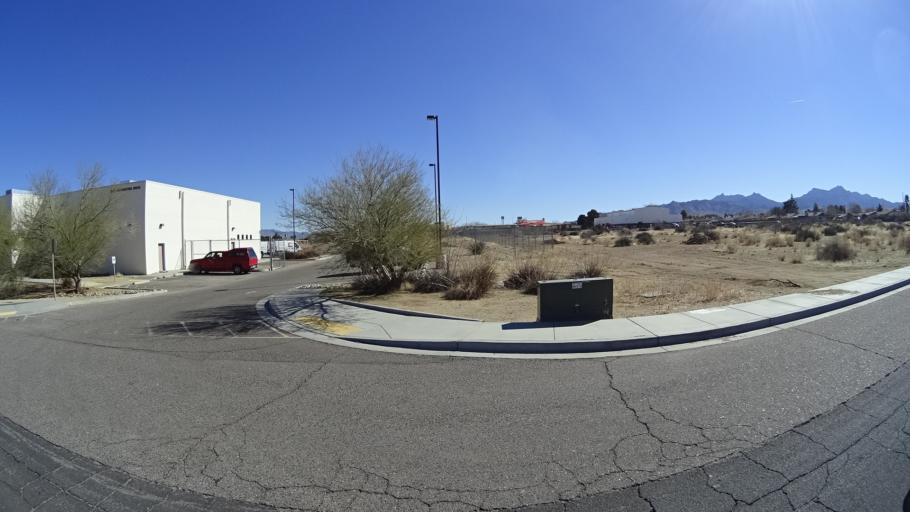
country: US
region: Arizona
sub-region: Mohave County
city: Kingman
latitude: 35.2153
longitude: -114.0203
